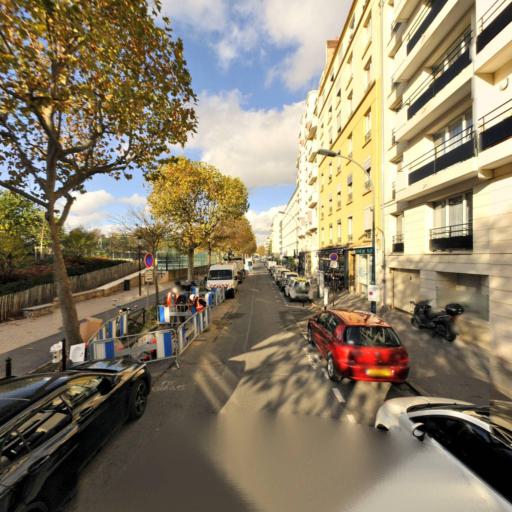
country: FR
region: Ile-de-France
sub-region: Departement des Hauts-de-Seine
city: Boulogne-Billancourt
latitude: 48.8278
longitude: 2.2421
